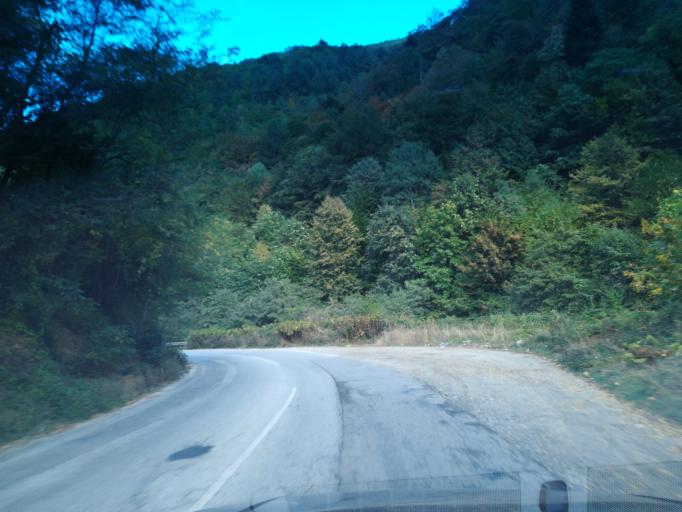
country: BG
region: Pazardzhik
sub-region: Obshtina Batak
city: Batak
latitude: 41.9898
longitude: 24.2529
